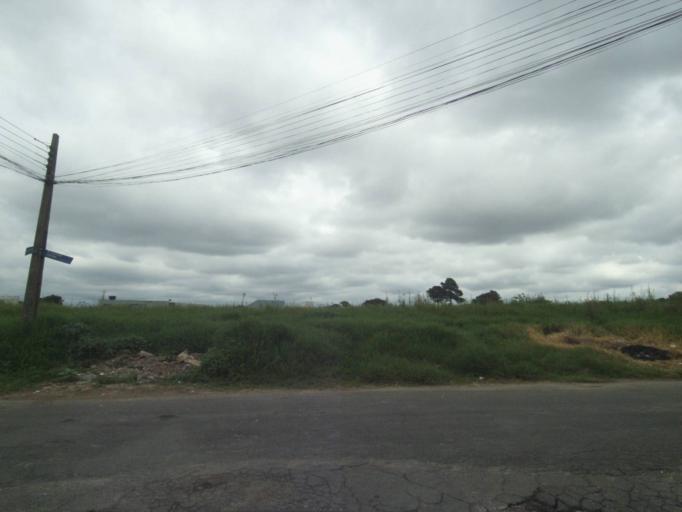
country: BR
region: Parana
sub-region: Pinhais
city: Pinhais
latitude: -25.4463
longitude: -49.2013
